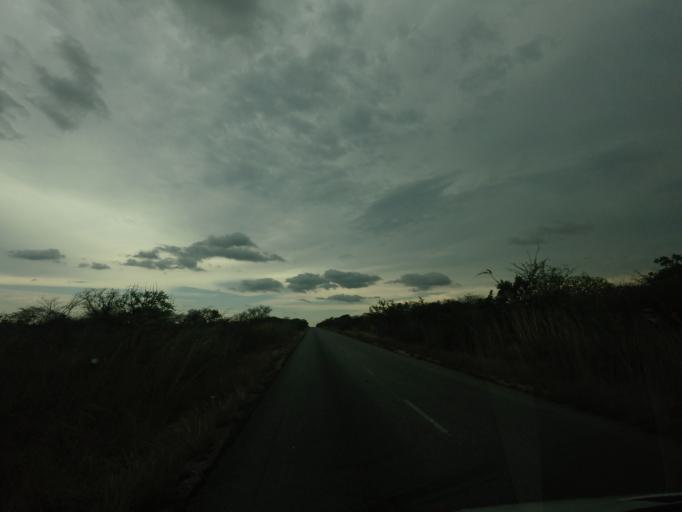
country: ZA
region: Limpopo
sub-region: Mopani District Municipality
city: Hoedspruit
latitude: -24.5321
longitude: 30.9976
